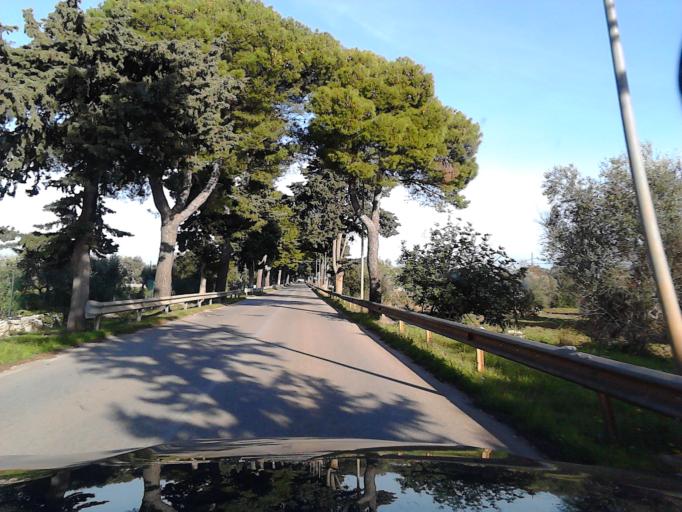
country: IT
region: Apulia
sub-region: Provincia di Bari
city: Mola di Bari
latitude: 41.0445
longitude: 17.0637
